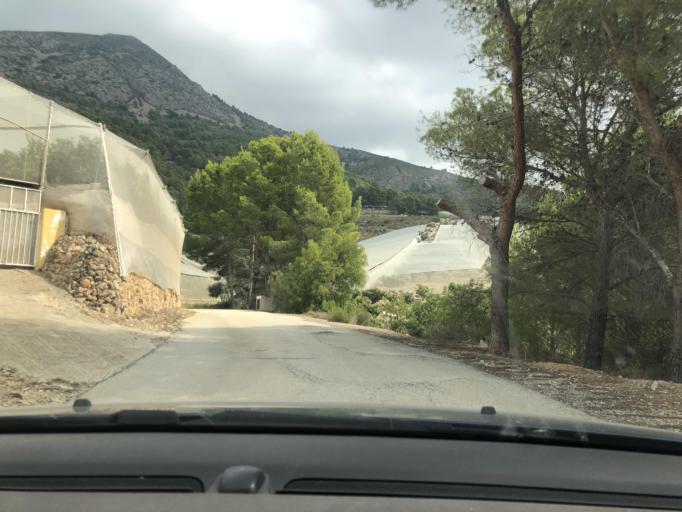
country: ES
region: Valencia
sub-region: Provincia de Alicante
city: Callosa d'En Sarria
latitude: 38.6540
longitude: -0.0913
